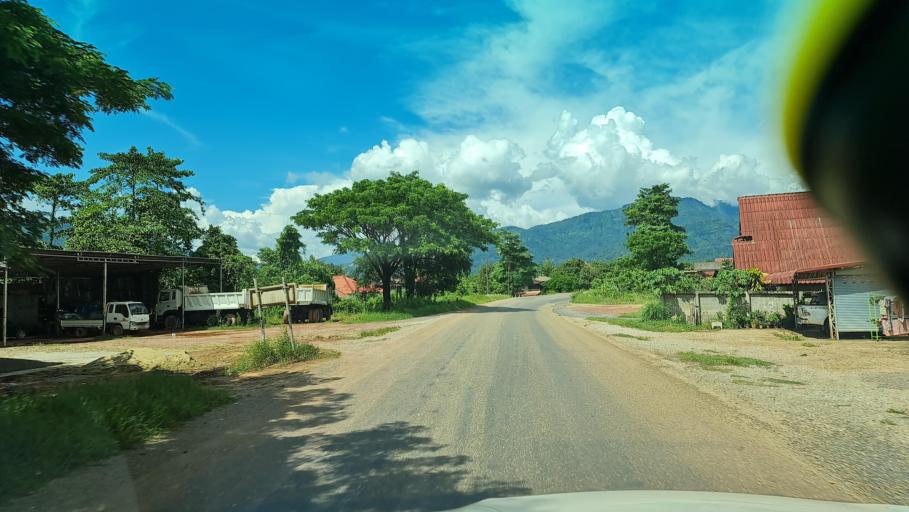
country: LA
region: Bolikhamxai
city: Ban Nahin
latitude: 18.3004
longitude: 104.1096
